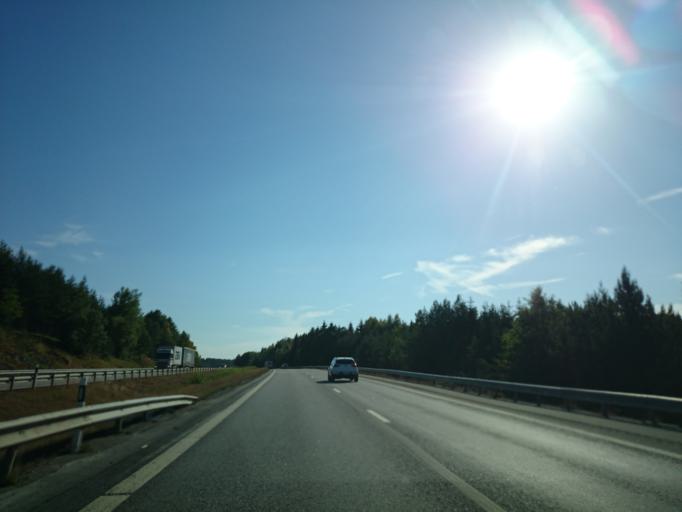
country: SE
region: Soedermanland
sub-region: Trosa Kommun
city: Vagnharad
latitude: 58.9710
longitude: 17.5144
